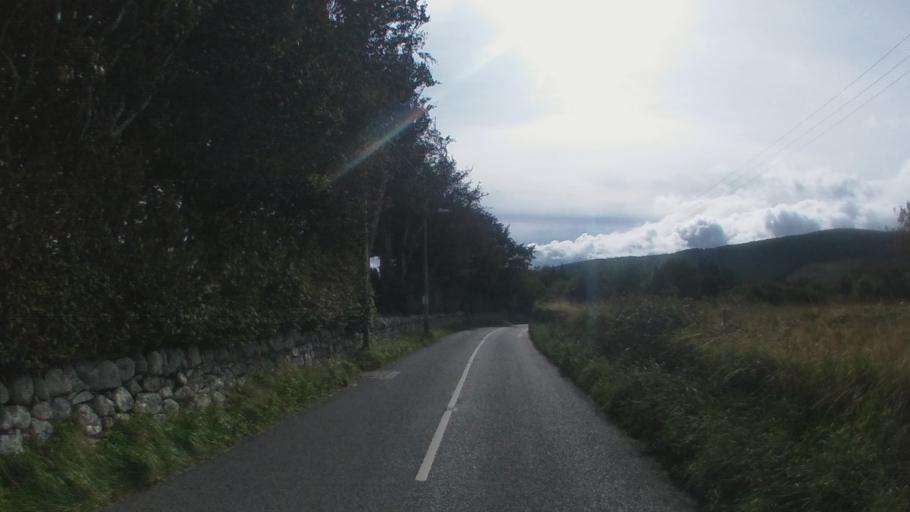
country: IE
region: Leinster
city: Sandyford
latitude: 53.2228
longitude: -6.2199
